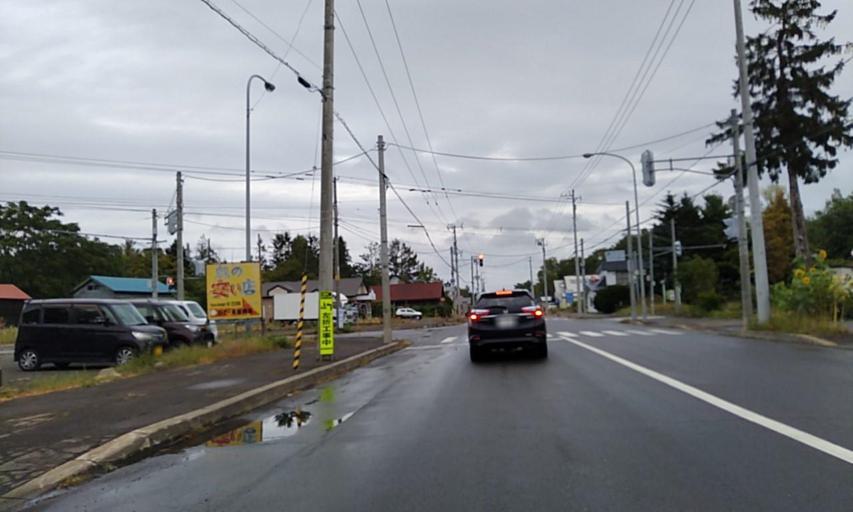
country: JP
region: Hokkaido
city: Kitami
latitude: 44.0812
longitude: 143.9444
